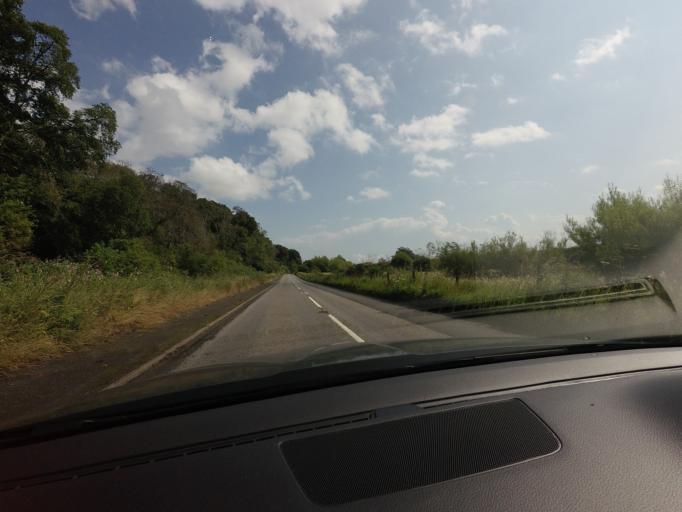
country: GB
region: Scotland
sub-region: Highland
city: Dingwall
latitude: 57.6072
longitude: -4.4155
